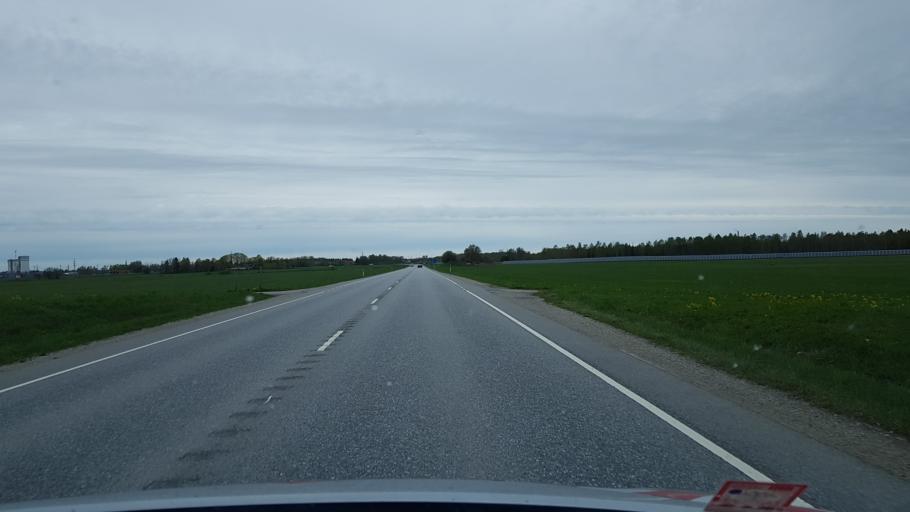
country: EE
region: Laeaene-Virumaa
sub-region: Someru vald
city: Someru
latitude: 59.3495
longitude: 26.4031
